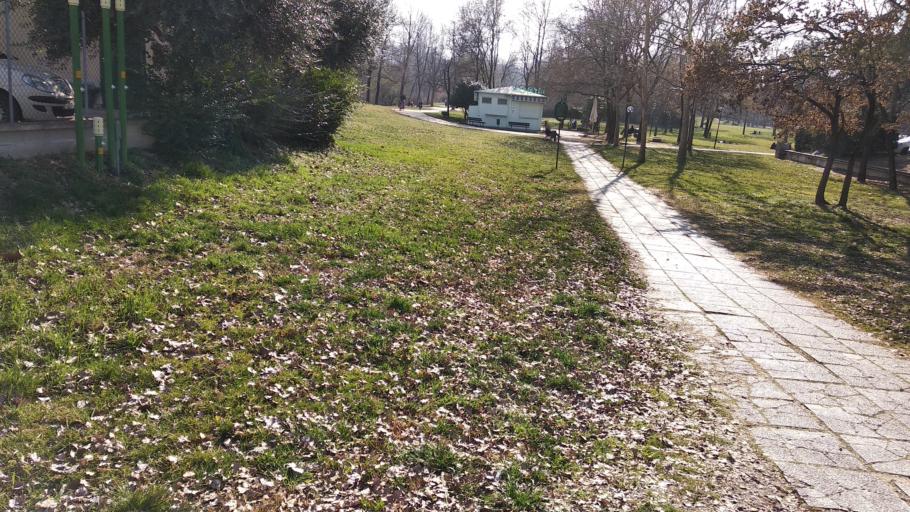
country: IT
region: Emilia-Romagna
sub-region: Provincia di Bologna
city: San Lazzaro
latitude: 44.4733
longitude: 11.4011
